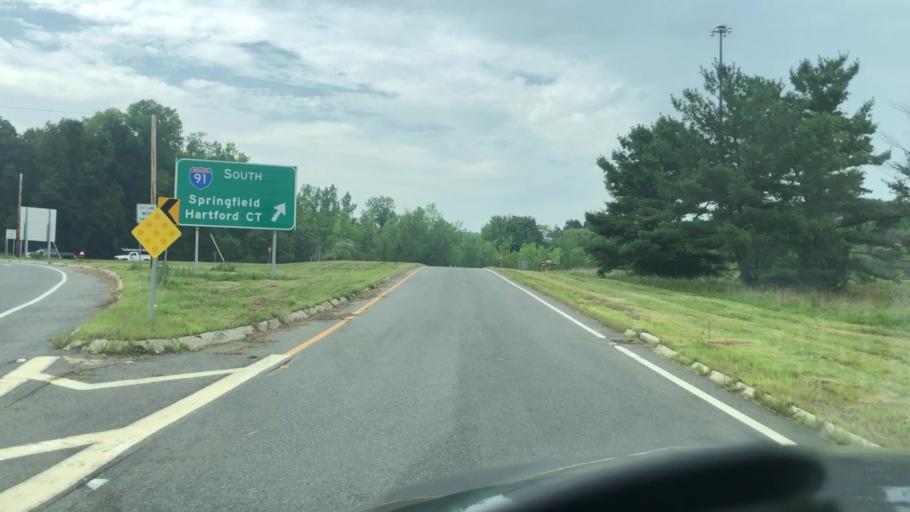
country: US
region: Massachusetts
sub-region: Hampden County
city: Holyoke
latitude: 42.2010
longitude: -72.6395
